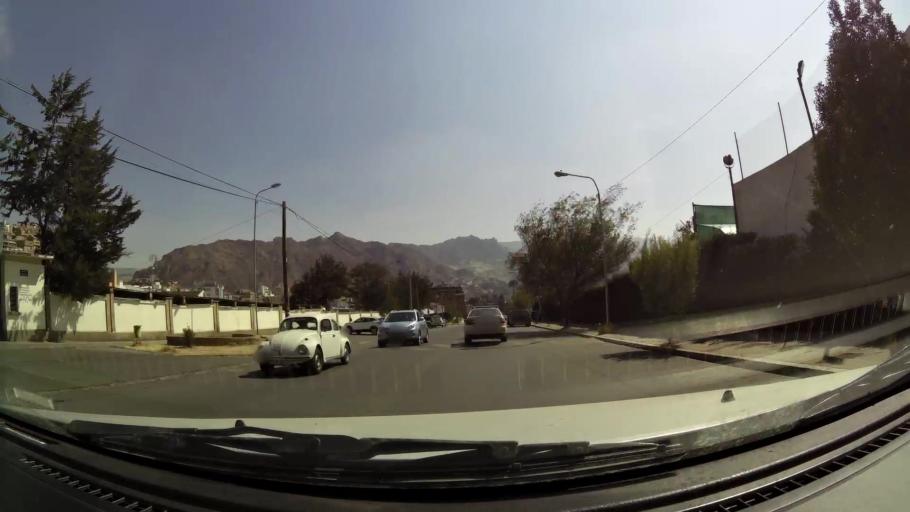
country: BO
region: La Paz
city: La Paz
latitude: -16.5443
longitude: -68.0817
